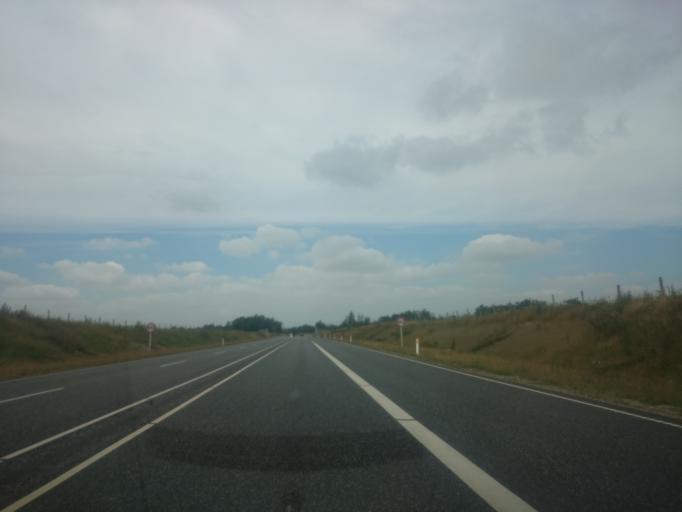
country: DK
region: South Denmark
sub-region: Vejle Kommune
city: Egtved
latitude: 55.7007
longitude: 9.3042
